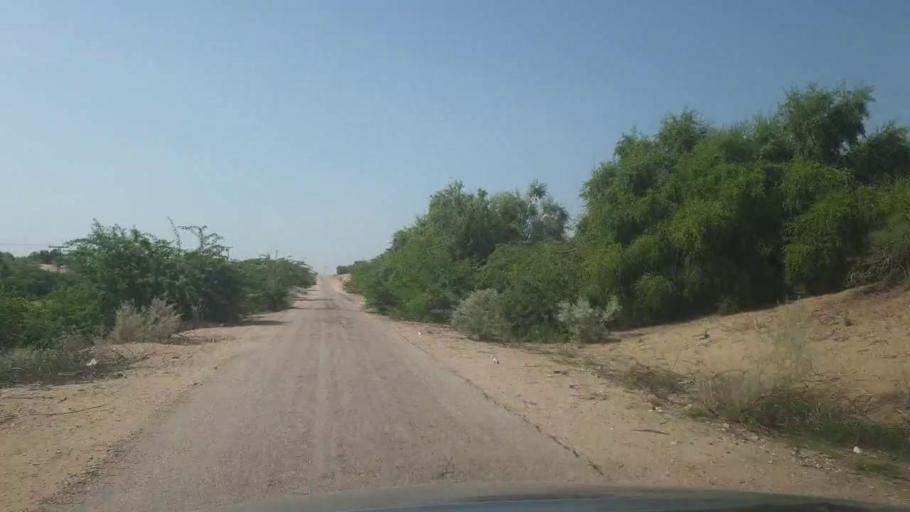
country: PK
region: Sindh
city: Rohri
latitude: 27.4271
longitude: 69.0787
